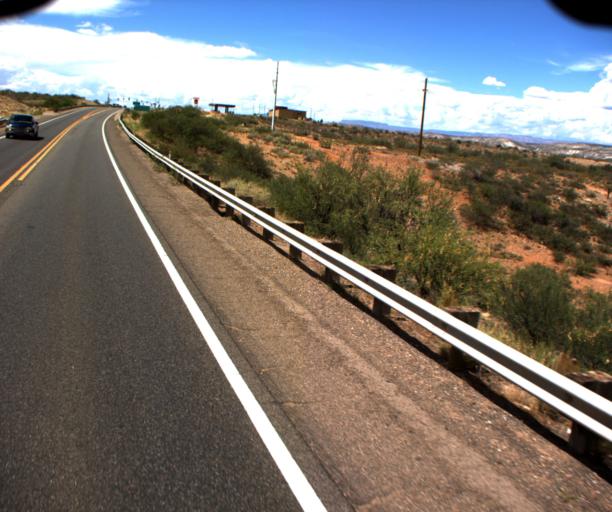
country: US
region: Arizona
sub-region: Yavapai County
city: Camp Verde
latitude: 34.6059
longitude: -111.9093
